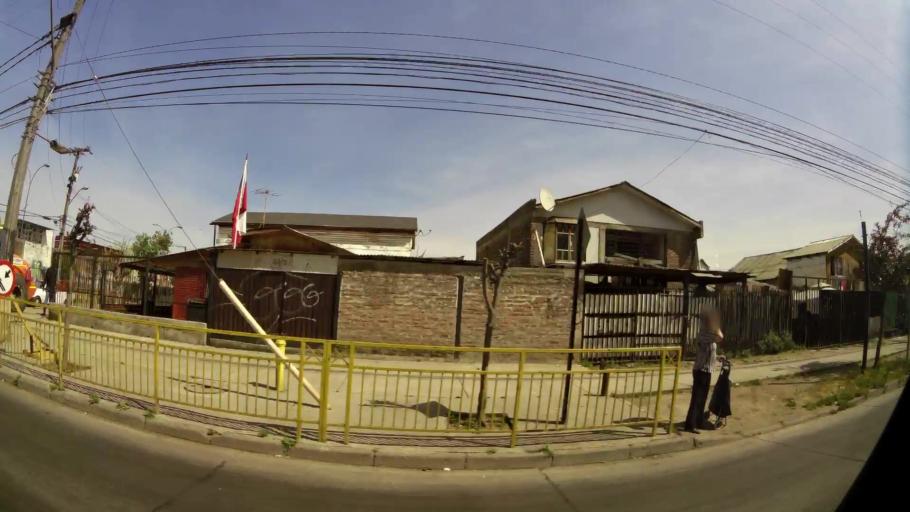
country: CL
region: Santiago Metropolitan
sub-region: Provincia de Santiago
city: Lo Prado
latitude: -33.4392
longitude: -70.7637
